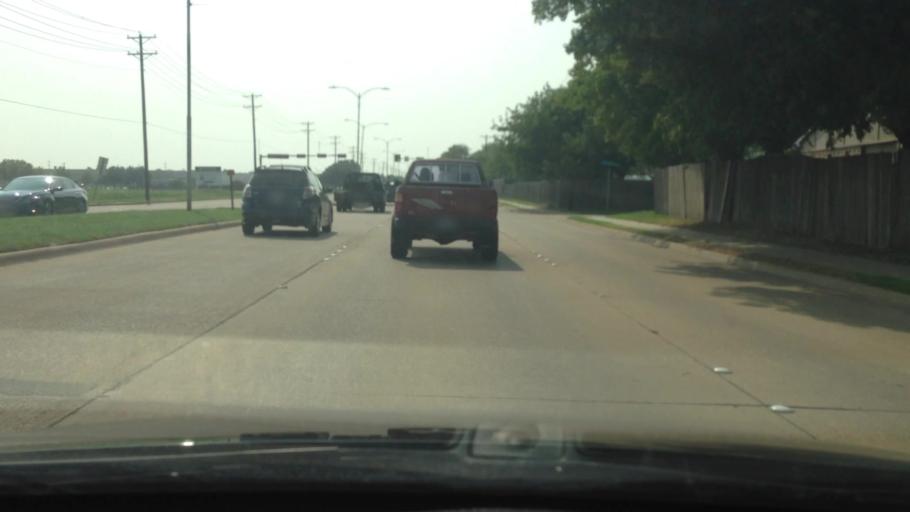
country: US
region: Texas
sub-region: Tarrant County
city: North Richland Hills
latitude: 32.8604
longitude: -97.2275
